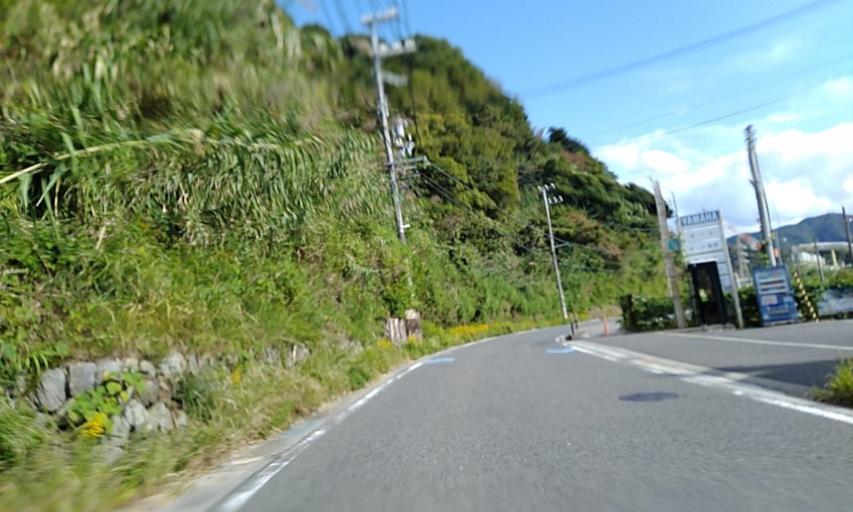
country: JP
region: Wakayama
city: Gobo
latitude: 33.9648
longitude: 135.1058
